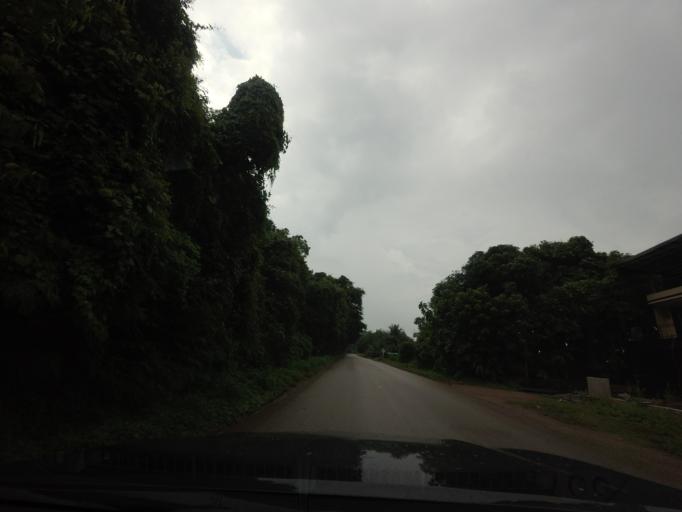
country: TH
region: Loei
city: Pak Chom
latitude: 18.1191
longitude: 101.9946
